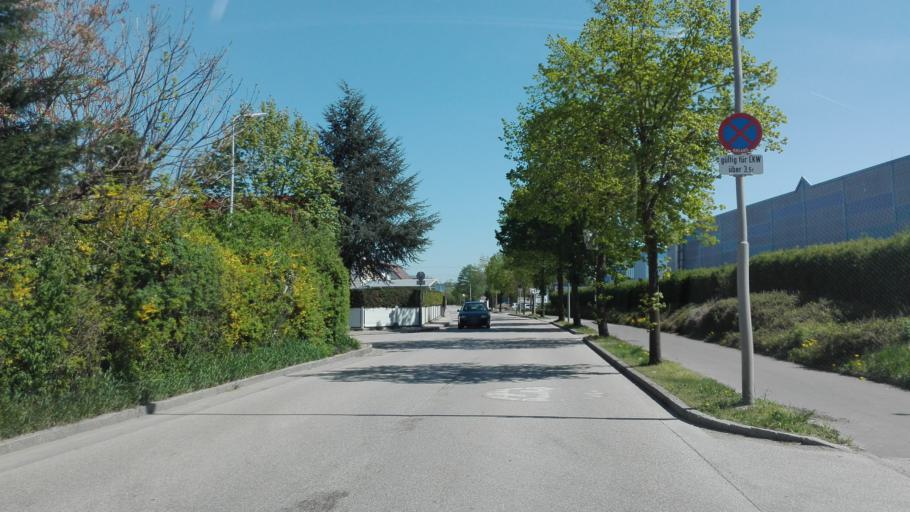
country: AT
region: Upper Austria
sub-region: Politischer Bezirk Linz-Land
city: Traun
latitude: 48.2100
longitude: 14.2113
